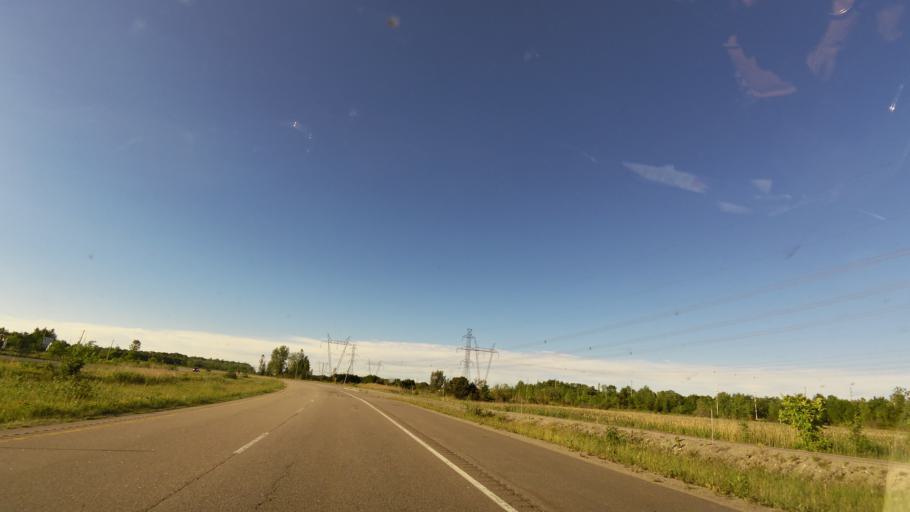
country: CA
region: Ontario
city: Midland
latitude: 44.7695
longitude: -79.6919
